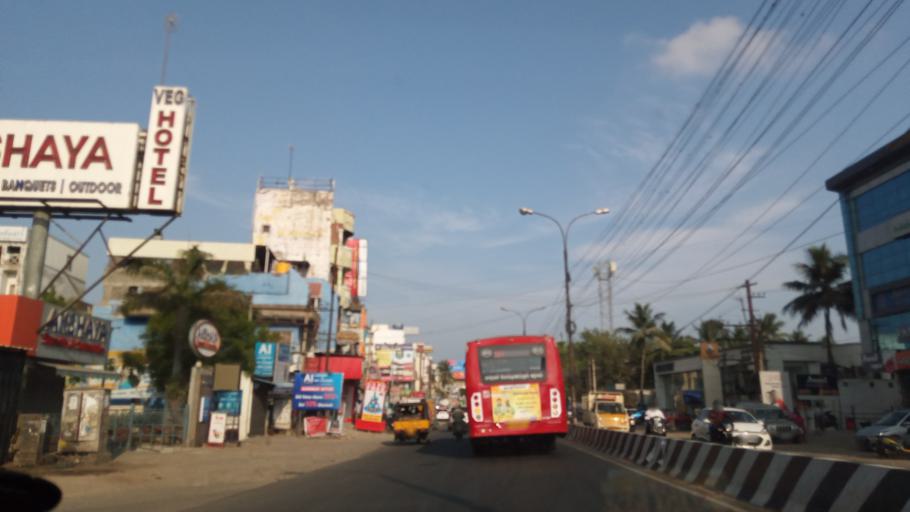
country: IN
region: Tamil Nadu
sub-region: Kancheepuram
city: Poonamalle
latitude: 13.0395
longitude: 80.1317
